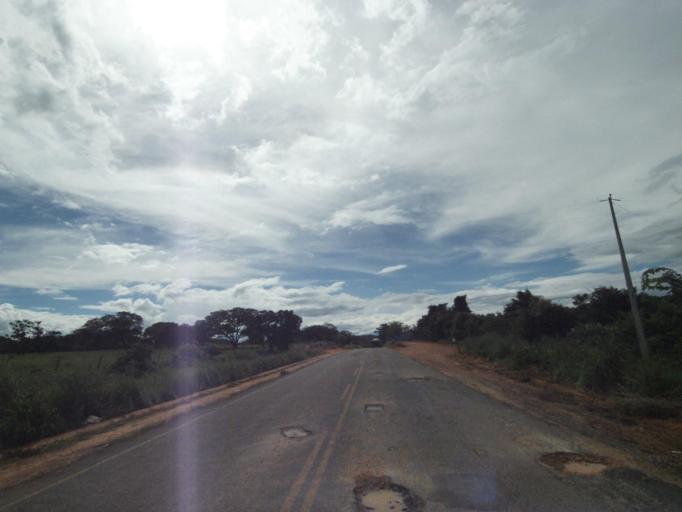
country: BR
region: Goias
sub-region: Pirenopolis
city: Pirenopolis
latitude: -15.7829
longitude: -49.0438
